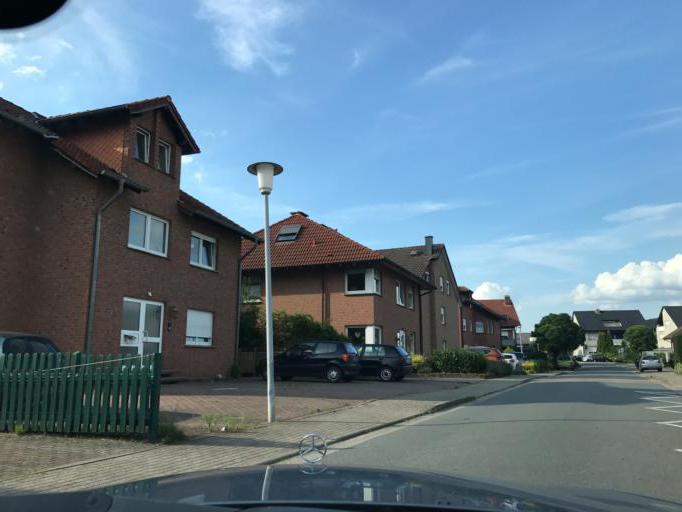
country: DE
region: Lower Saxony
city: Hasbergen
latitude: 52.2010
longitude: 7.9379
